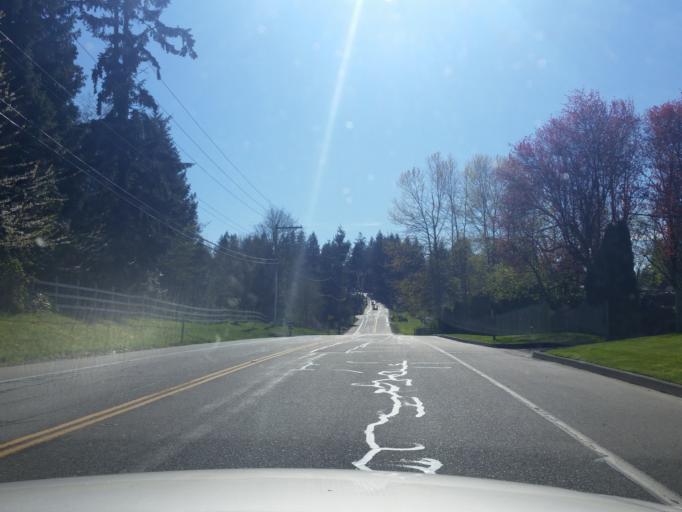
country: US
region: Washington
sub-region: Snohomish County
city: Silver Firs
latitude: 47.8828
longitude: -122.1583
